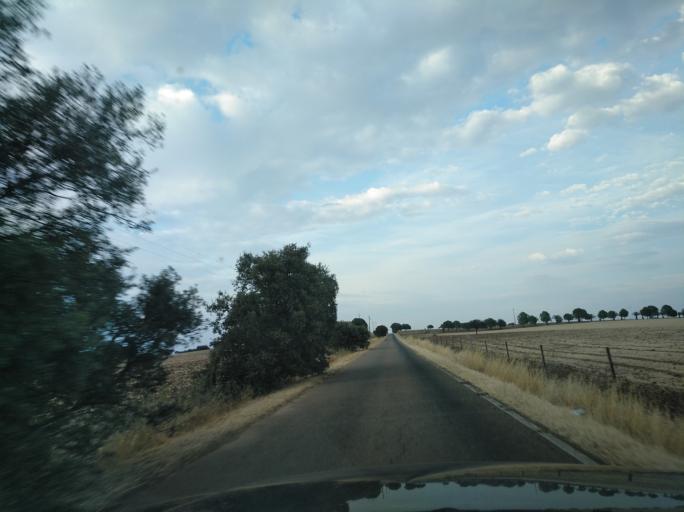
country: PT
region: Portalegre
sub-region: Campo Maior
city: Campo Maior
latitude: 38.9933
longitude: -6.9975
